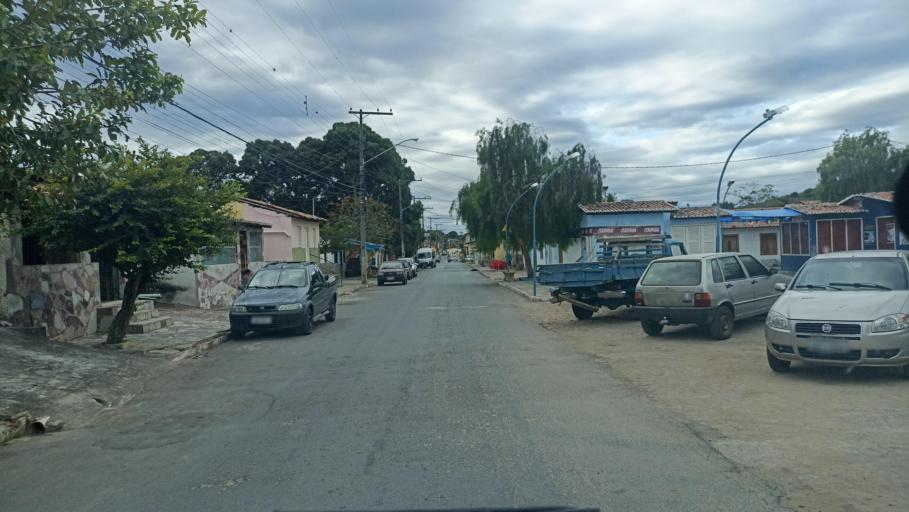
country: BR
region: Bahia
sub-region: Andarai
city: Vera Cruz
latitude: -12.8140
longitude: -41.3319
